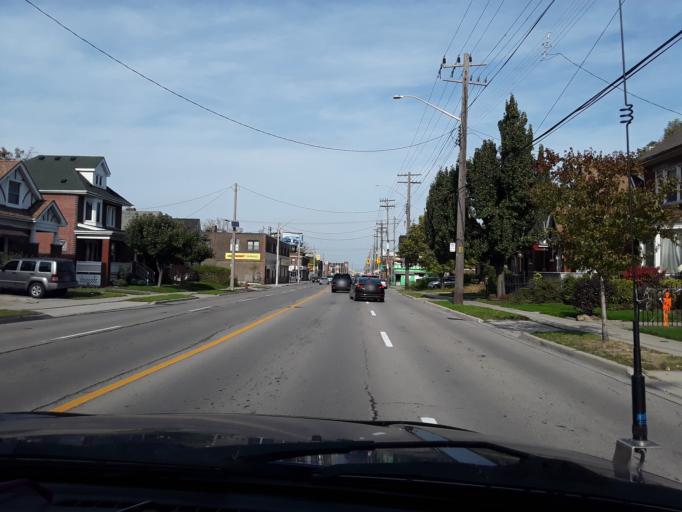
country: CA
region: Ontario
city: Hamilton
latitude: 43.2394
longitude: -79.8103
